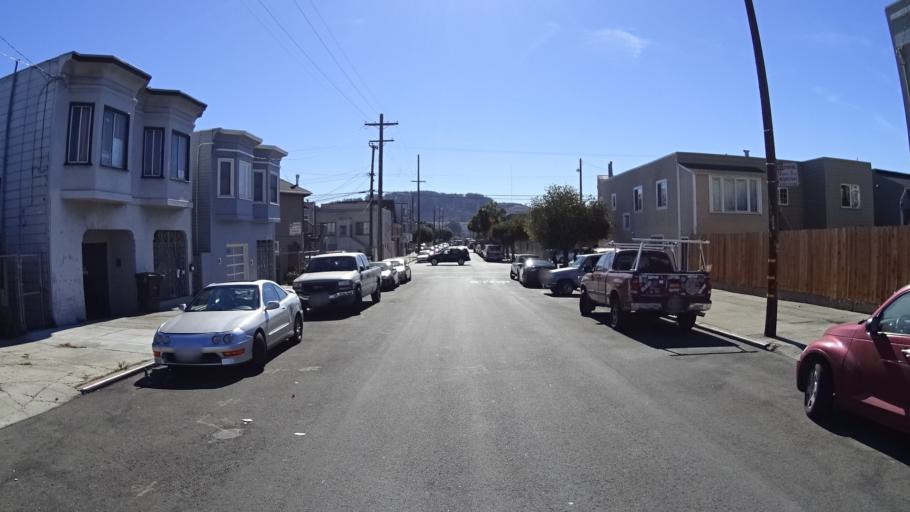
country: US
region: California
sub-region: San Mateo County
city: Brisbane
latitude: 37.7281
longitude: -122.3819
